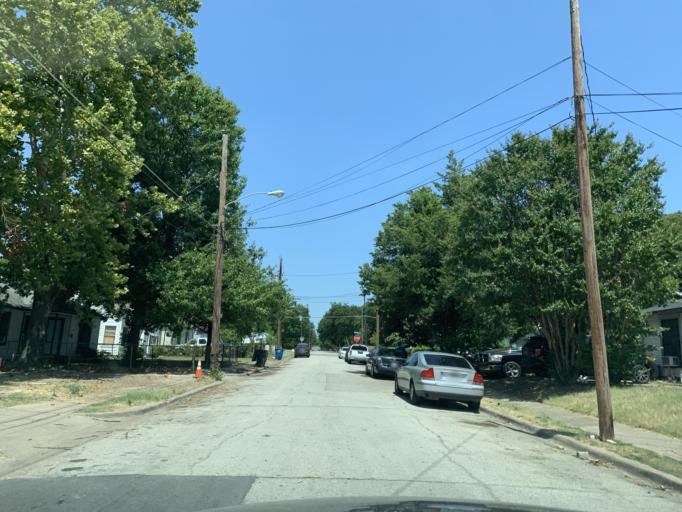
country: US
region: Texas
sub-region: Dallas County
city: Hutchins
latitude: 32.6878
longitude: -96.7916
